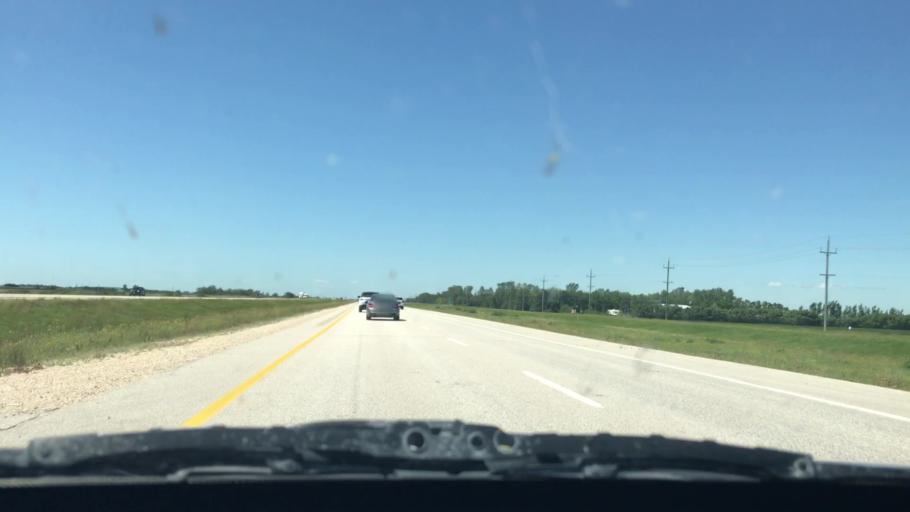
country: CA
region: Manitoba
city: Steinbach
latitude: 49.7394
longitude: -96.7419
